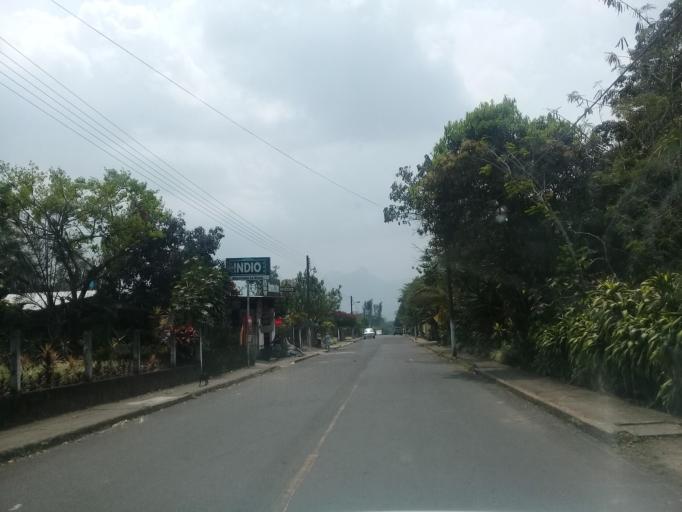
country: MX
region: Veracruz
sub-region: Cordoba
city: Fredepo
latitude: 18.8589
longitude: -96.9915
